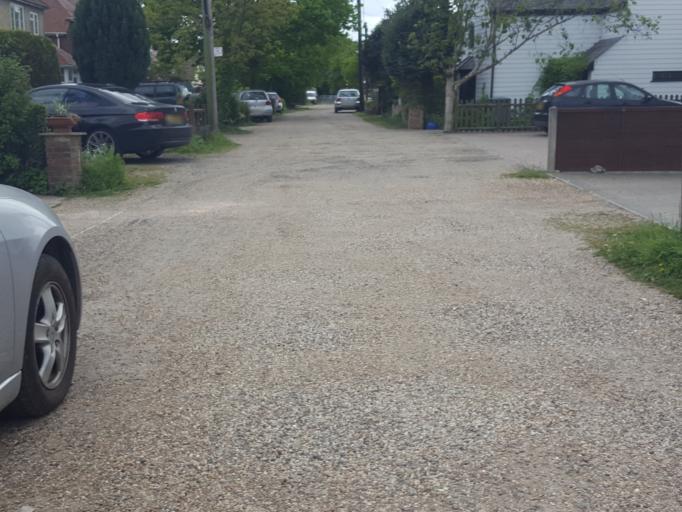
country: GB
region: England
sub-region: Essex
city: Frinton-on-Sea
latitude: 51.8437
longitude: 1.2093
